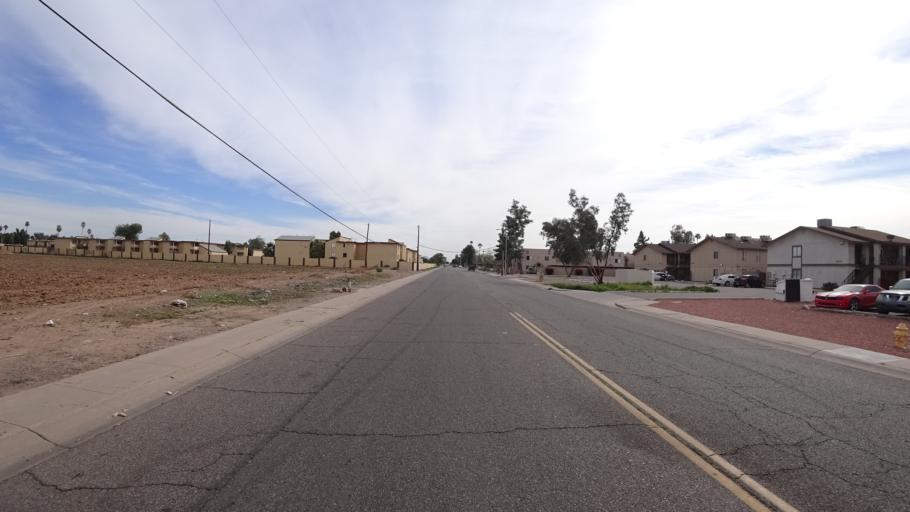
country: US
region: Arizona
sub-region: Maricopa County
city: Glendale
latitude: 33.5347
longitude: -112.2018
